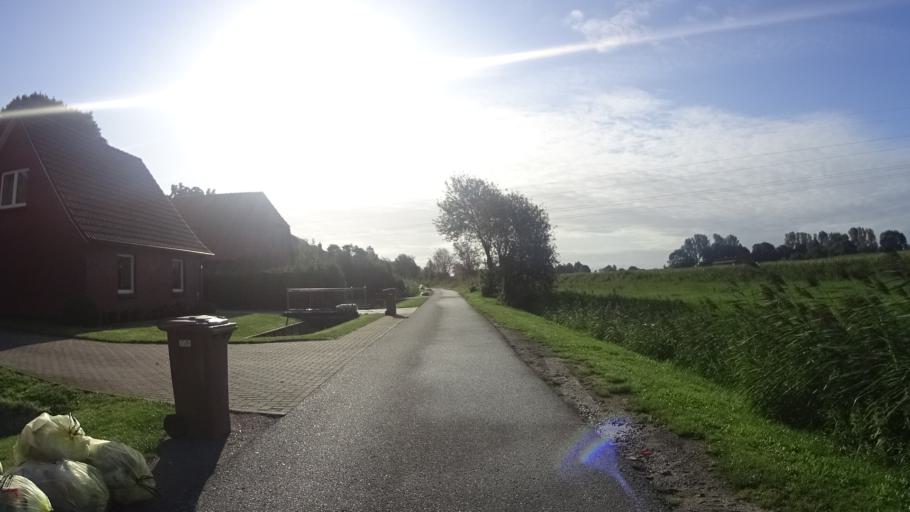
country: DE
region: Lower Saxony
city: Nordenham
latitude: 53.4963
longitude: 8.4342
